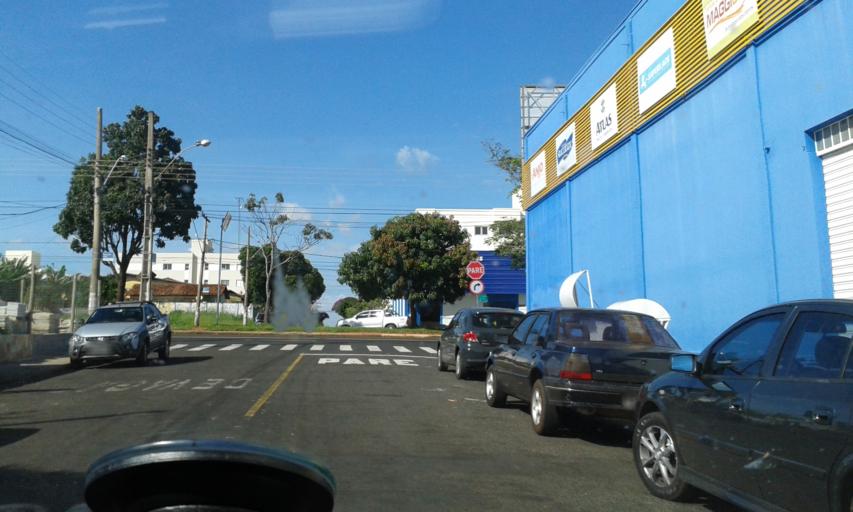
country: BR
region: Minas Gerais
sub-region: Uberlandia
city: Uberlandia
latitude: -18.9193
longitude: -48.2436
